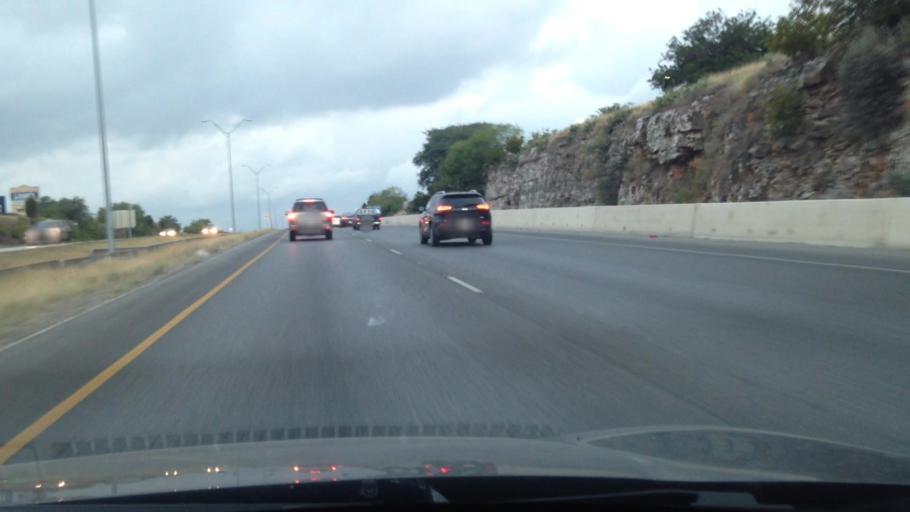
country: US
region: Texas
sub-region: Bexar County
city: Hollywood Park
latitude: 29.6092
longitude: -98.5099
